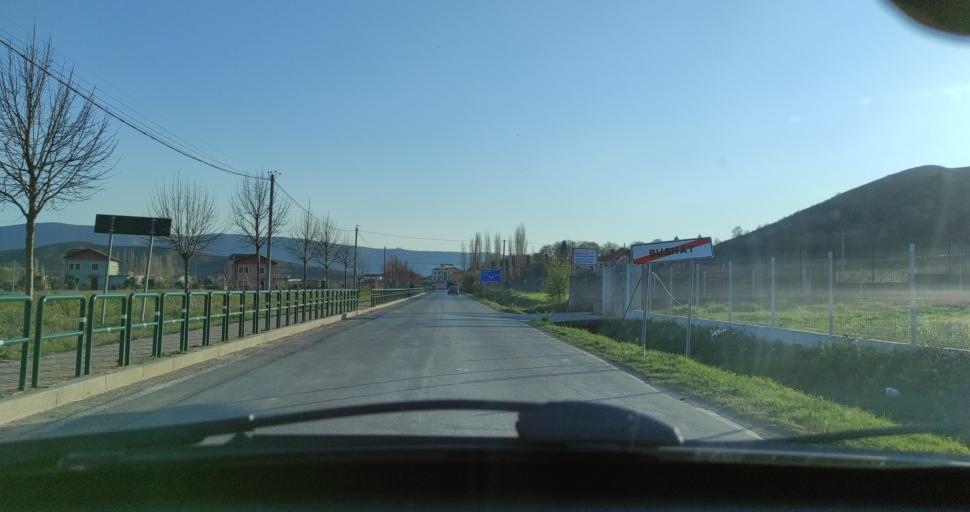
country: AL
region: Shkoder
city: Vukatane
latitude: 41.9556
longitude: 19.5312
